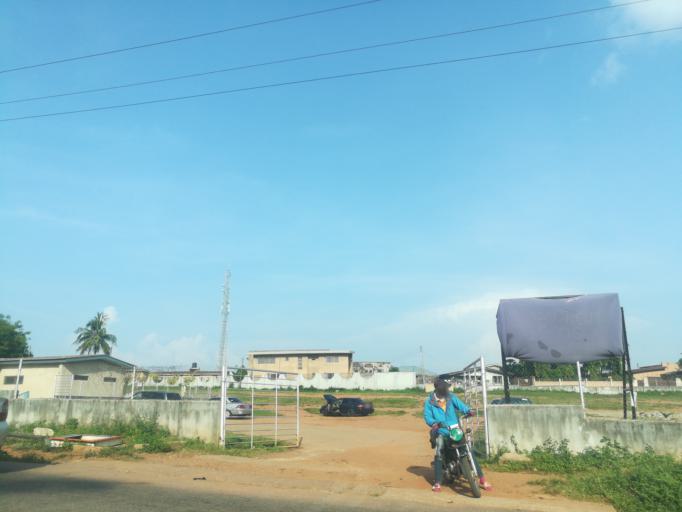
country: NG
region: Oyo
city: Moniya
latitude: 7.4998
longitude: 3.9134
